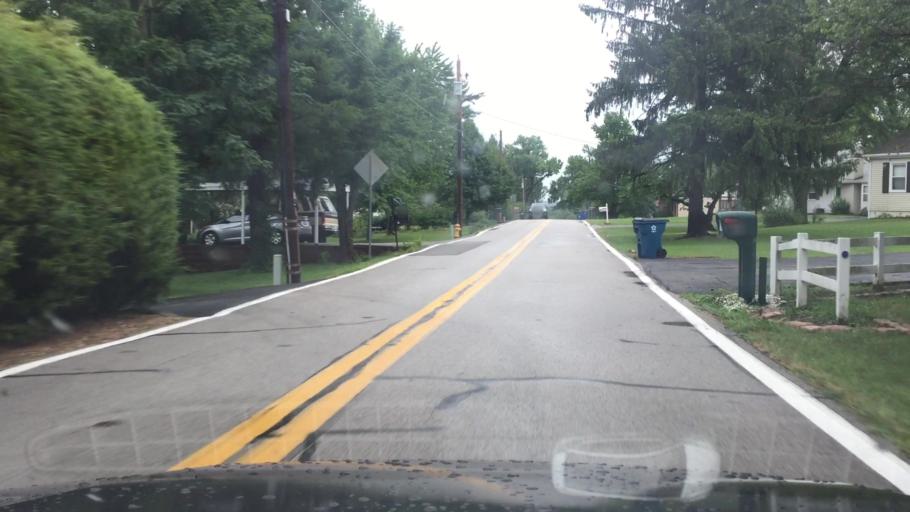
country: US
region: Missouri
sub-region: Saint Louis County
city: Concord
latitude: 38.5065
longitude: -90.3518
